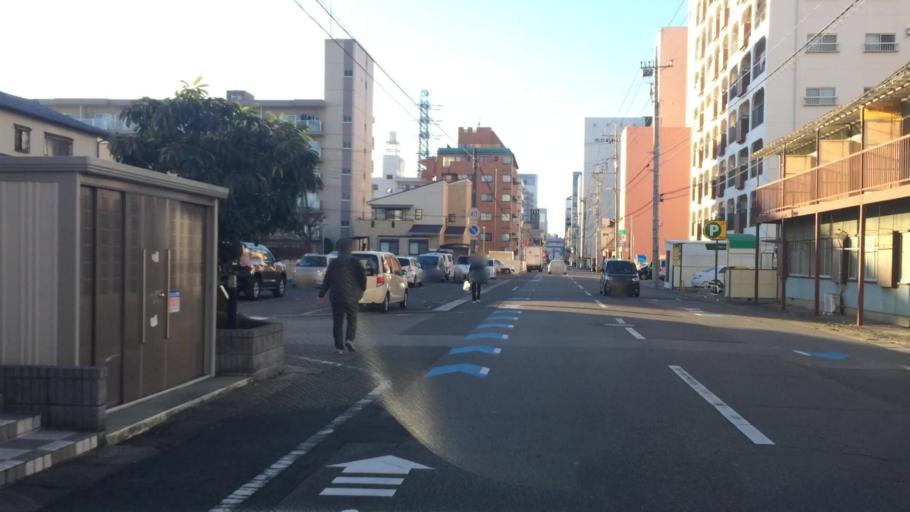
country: JP
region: Tochigi
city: Utsunomiya-shi
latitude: 36.5574
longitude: 139.9072
